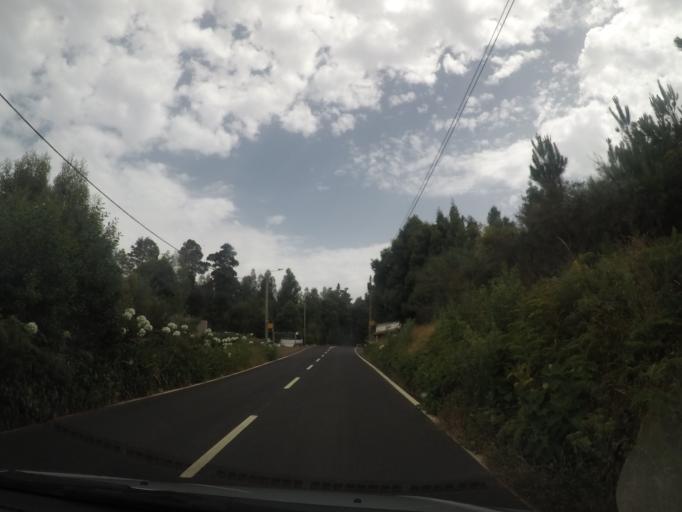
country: PT
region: Madeira
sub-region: Santa Cruz
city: Camacha
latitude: 32.6918
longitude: -16.8391
